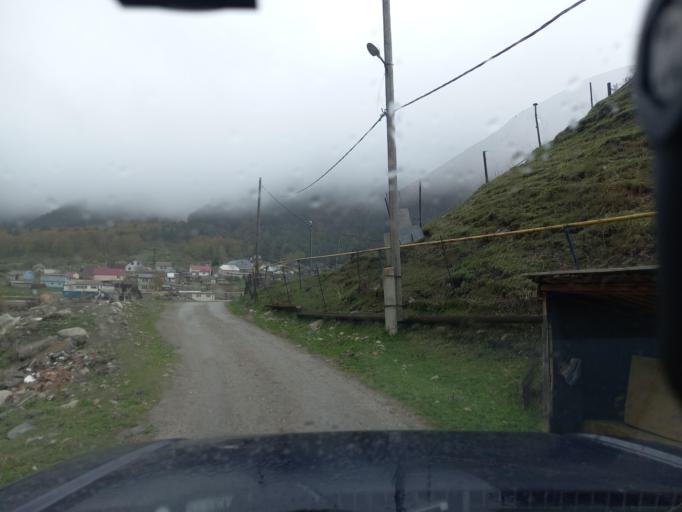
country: RU
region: Kabardino-Balkariya
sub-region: El'brusskiy Rayon
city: El'brus
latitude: 43.2619
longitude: 42.6494
